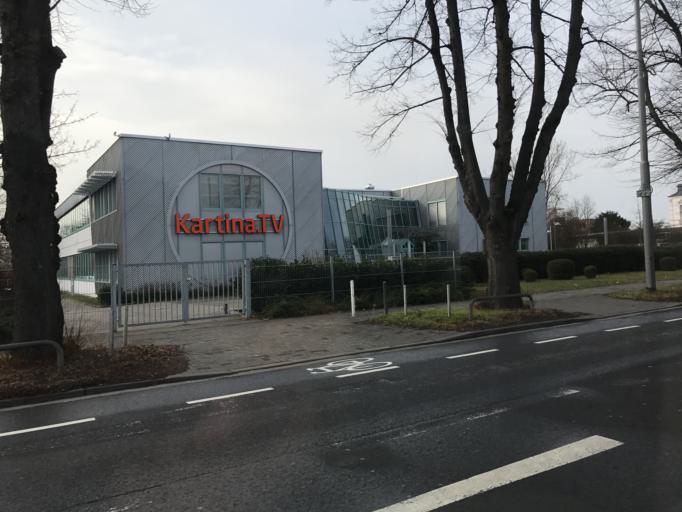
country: DE
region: Rheinland-Pfalz
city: Budenheim
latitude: 50.0432
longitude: 8.2084
